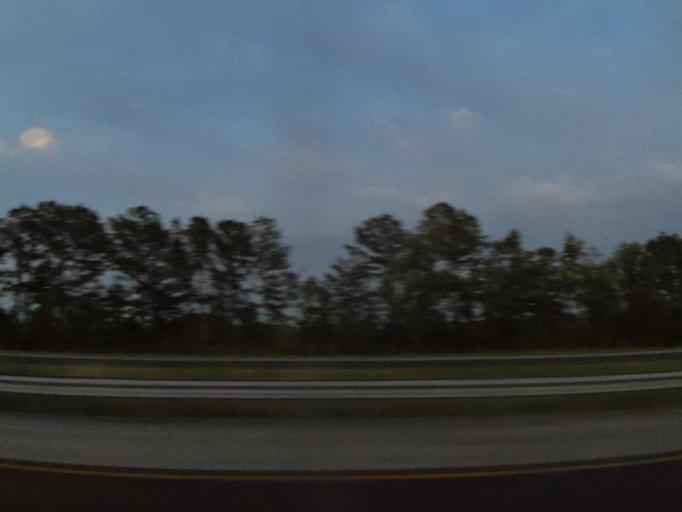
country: US
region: Georgia
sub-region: Liberty County
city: Midway
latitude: 31.6674
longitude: -81.3926
